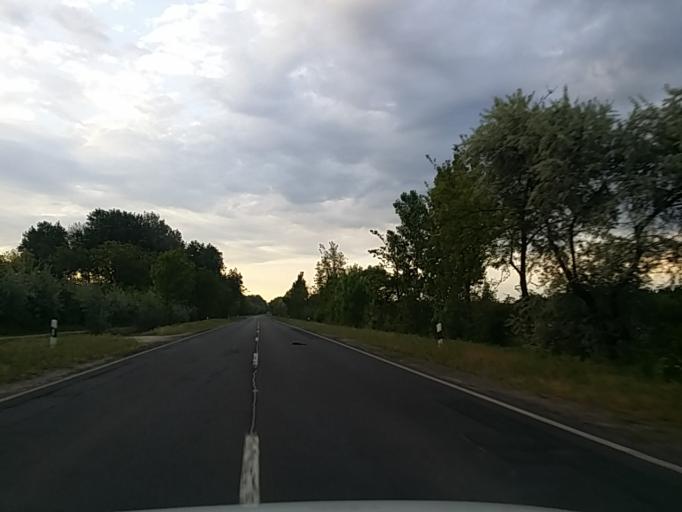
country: HU
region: Pest
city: Taborfalva
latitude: 47.0585
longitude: 19.5121
